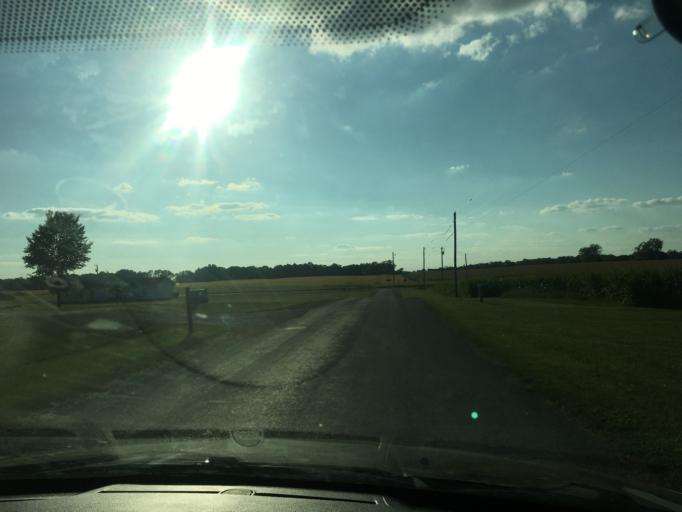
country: US
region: Ohio
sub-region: Logan County
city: West Liberty
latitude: 40.1852
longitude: -83.7604
